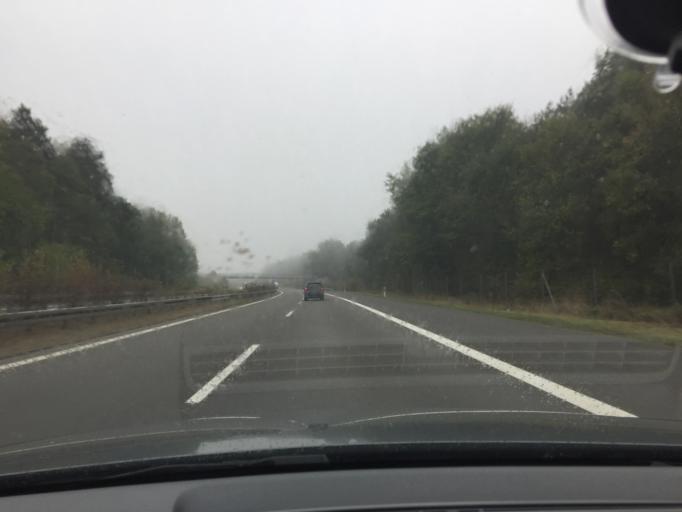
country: DE
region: Brandenburg
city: Bronkow
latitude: 51.6718
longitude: 13.9021
